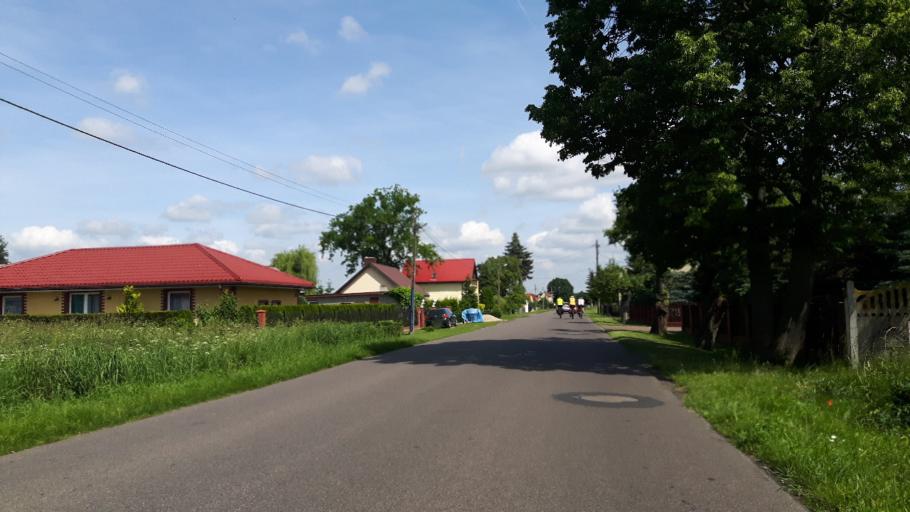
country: PL
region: West Pomeranian Voivodeship
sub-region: Powiat goleniowski
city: Goleniow
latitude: 53.4916
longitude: 14.7770
